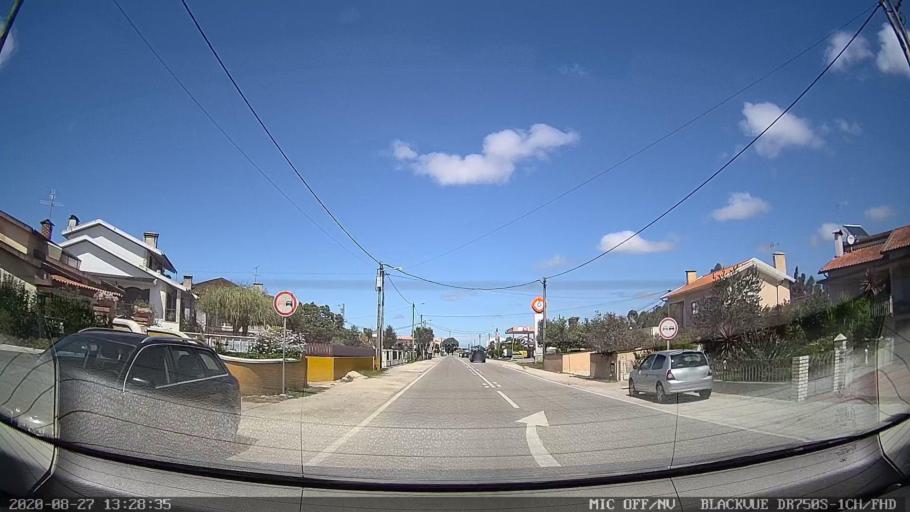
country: PT
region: Aveiro
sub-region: Vagos
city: Vagos
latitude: 40.5187
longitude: -8.6788
